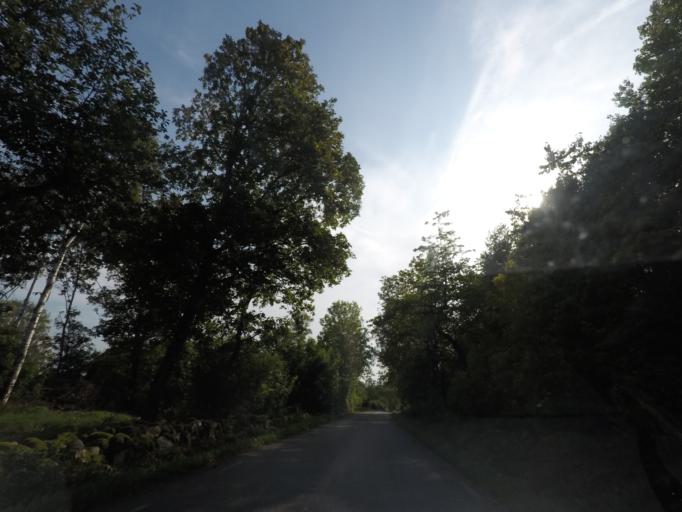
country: SE
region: Vaestmanland
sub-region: Kungsors Kommun
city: Kungsoer
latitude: 59.5051
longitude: 16.1561
